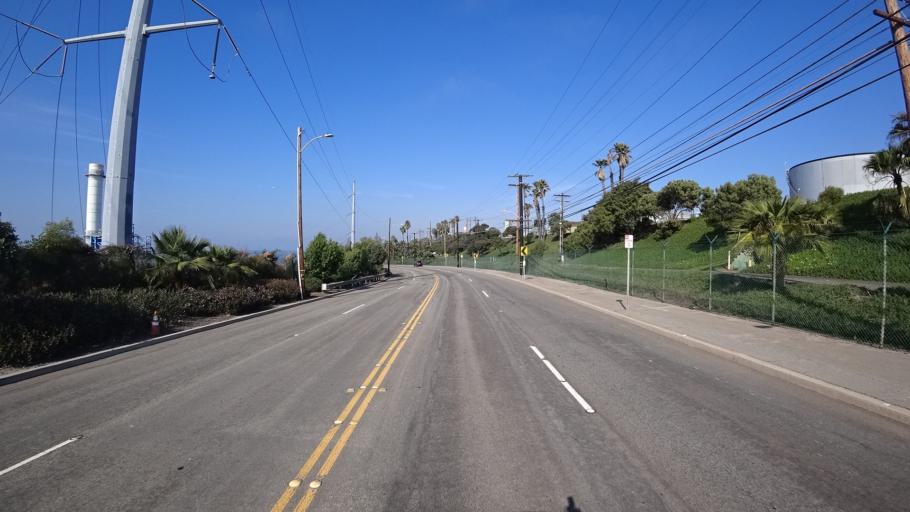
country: US
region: California
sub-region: Los Angeles County
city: El Segundo
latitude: 33.9108
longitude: -118.4236
